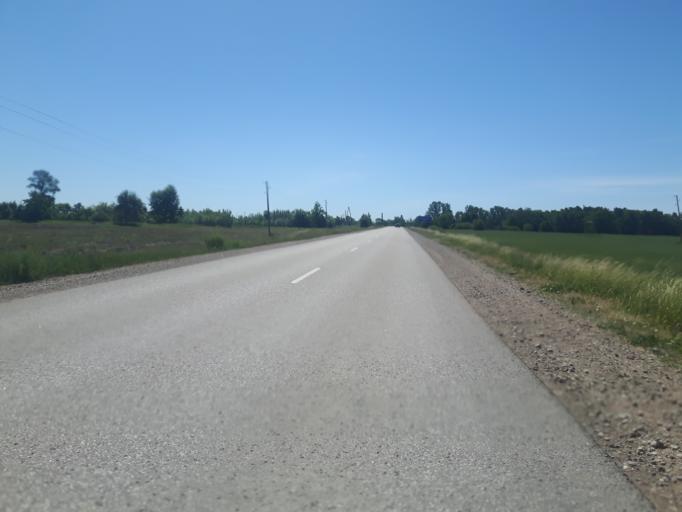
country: LV
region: Durbe
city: Liegi
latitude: 56.5701
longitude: 21.2710
